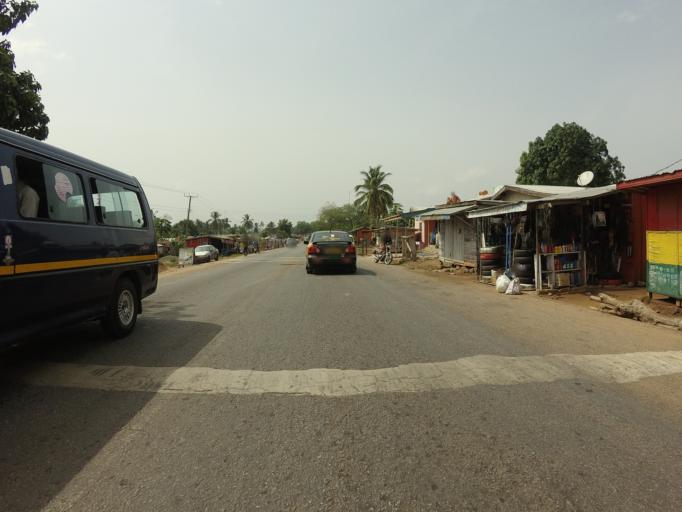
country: GH
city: Akropong
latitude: 6.2472
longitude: 0.1280
